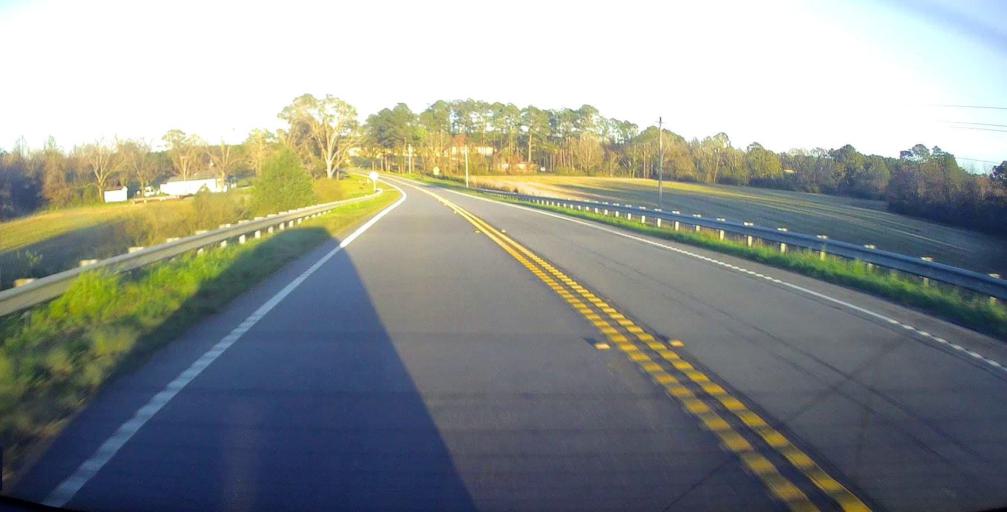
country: US
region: Georgia
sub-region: Crisp County
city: Cordele
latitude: 31.9501
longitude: -83.7022
